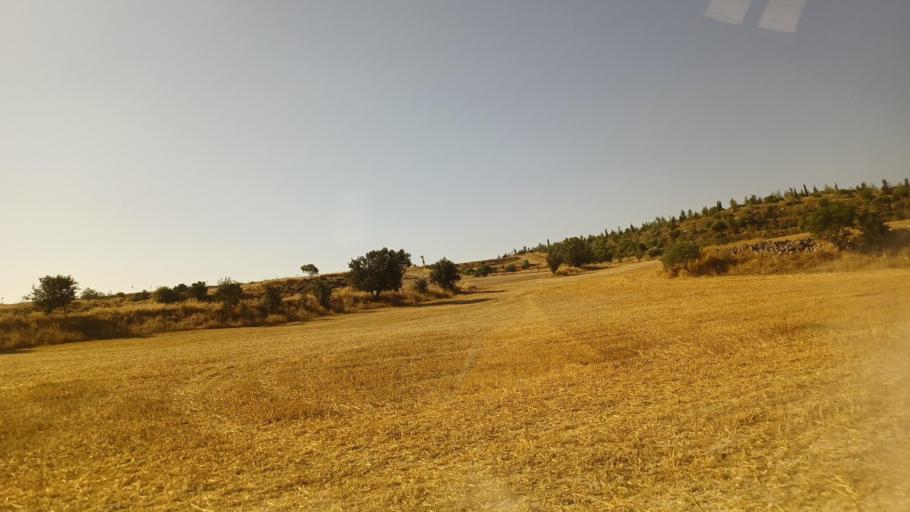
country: CY
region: Larnaka
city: Athienou
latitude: 35.0277
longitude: 33.5444
